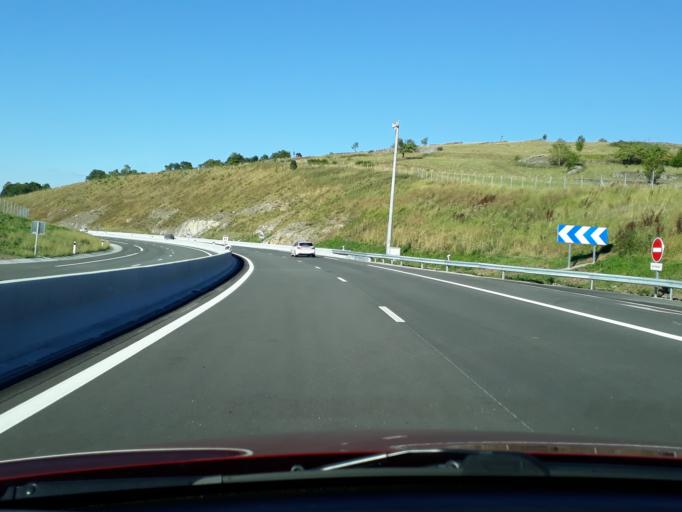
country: FR
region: Auvergne
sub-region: Departement de la Haute-Loire
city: Vals-pres-le-Puy
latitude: 45.0191
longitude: 3.8996
